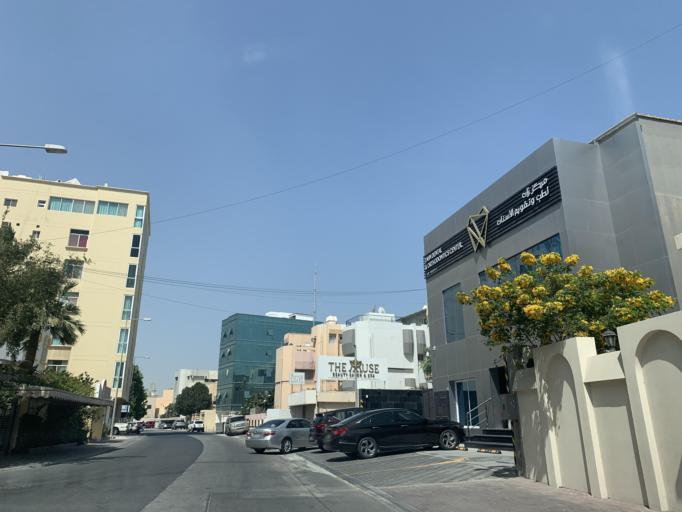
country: BH
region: Manama
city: Manama
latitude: 26.2061
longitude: 50.5813
